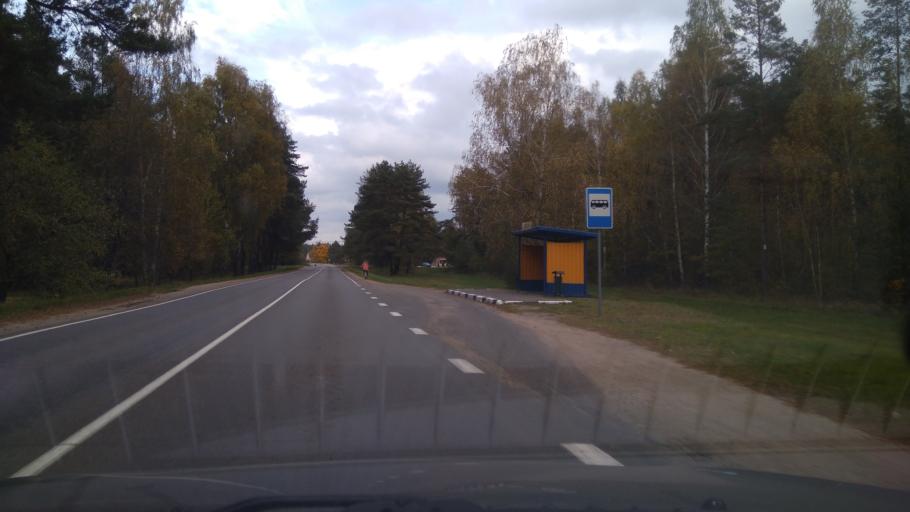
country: BY
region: Minsk
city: Svislach
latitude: 53.6482
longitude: 27.9223
